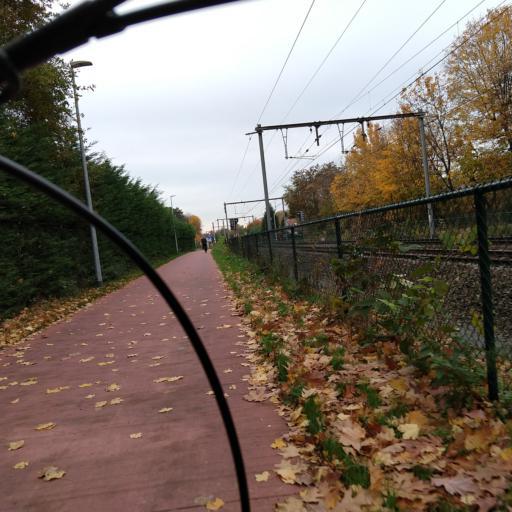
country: BE
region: Flanders
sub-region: Provincie Antwerpen
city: Kalmthout
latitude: 51.3737
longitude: 4.4653
